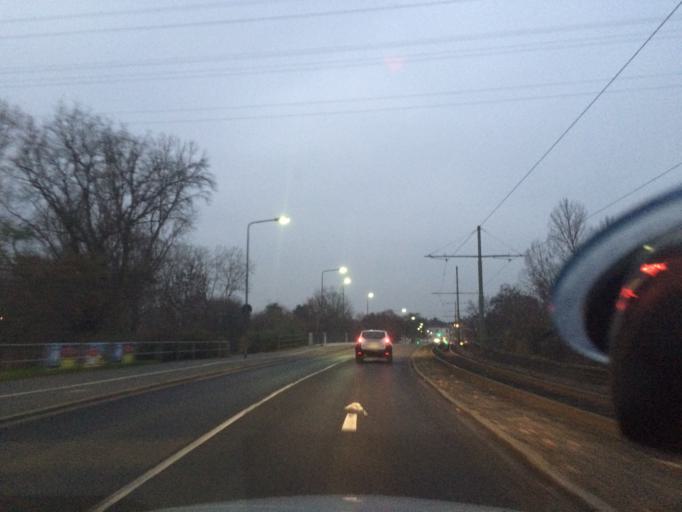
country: DE
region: Hesse
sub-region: Regierungsbezirk Darmstadt
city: Eschborn
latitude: 50.0996
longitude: 8.5622
